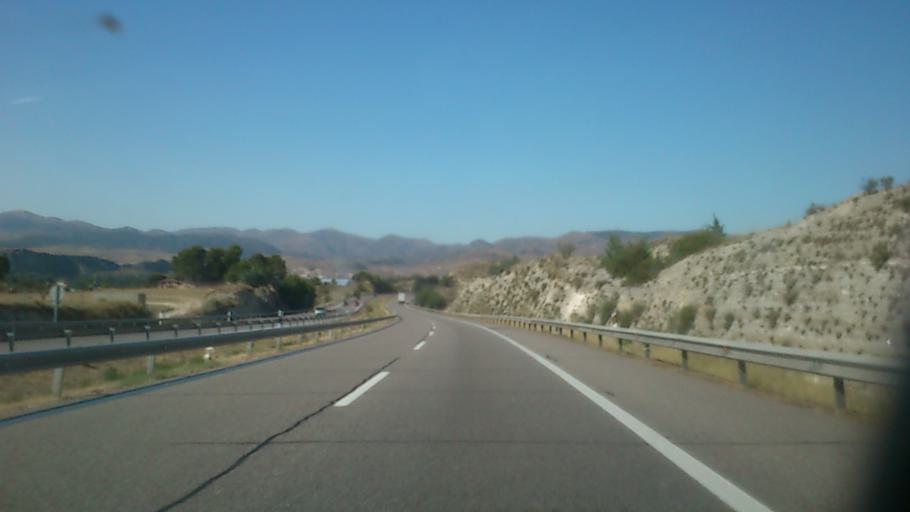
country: ES
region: Aragon
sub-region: Provincia de Zaragoza
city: Calatayud
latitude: 41.3400
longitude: -1.6317
